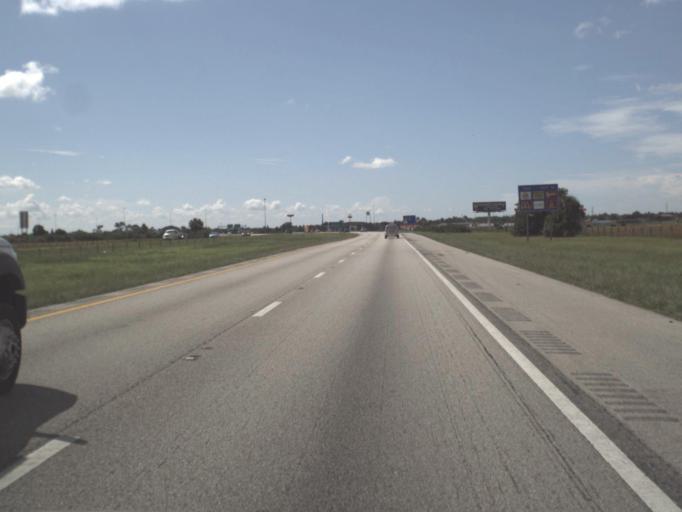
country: US
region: Florida
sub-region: Charlotte County
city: Punta Gorda
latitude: 26.9052
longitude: -82.0090
